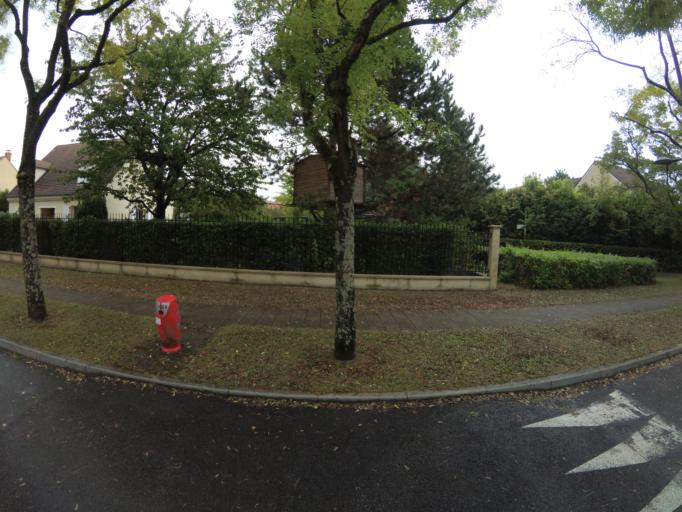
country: FR
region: Ile-de-France
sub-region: Departement de Seine-et-Marne
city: Bussy-Saint-Georges
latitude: 48.8442
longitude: 2.7096
